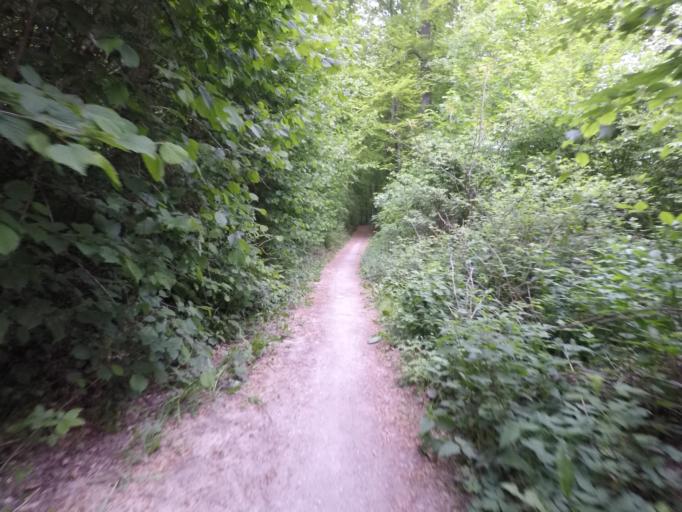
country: DE
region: North Rhine-Westphalia
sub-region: Regierungsbezirk Detmold
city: Bad Salzuflen
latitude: 52.1045
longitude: 8.7554
